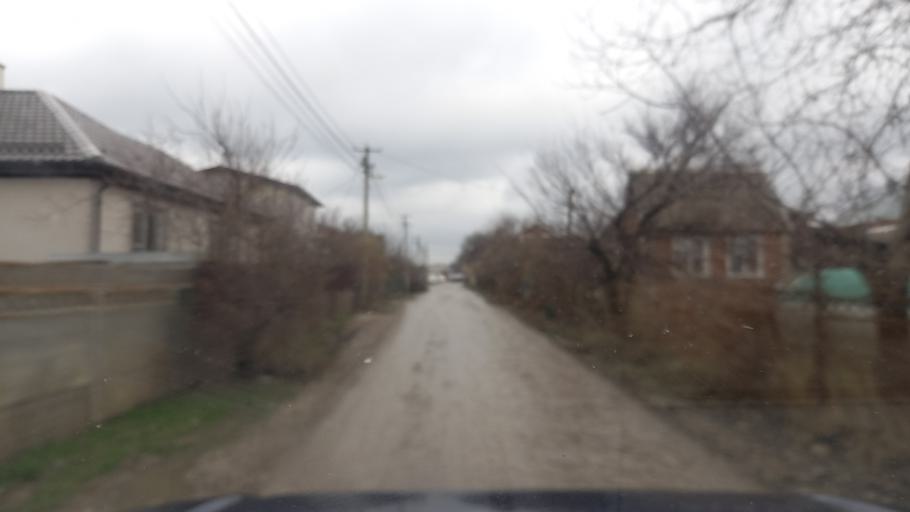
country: RU
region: Krasnodarskiy
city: Pashkovskiy
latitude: 45.0576
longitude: 39.1738
